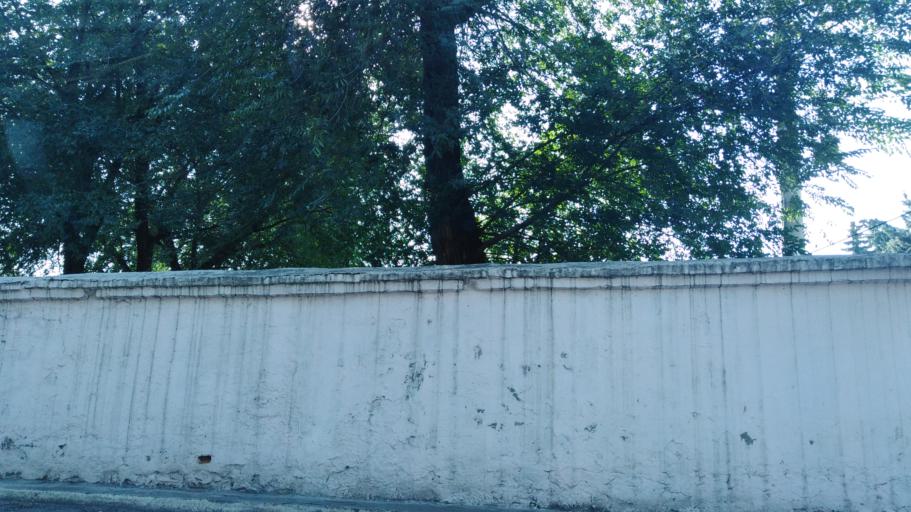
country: RU
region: Stavropol'skiy
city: Pyatigorsk
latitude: 44.0393
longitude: 43.0619
